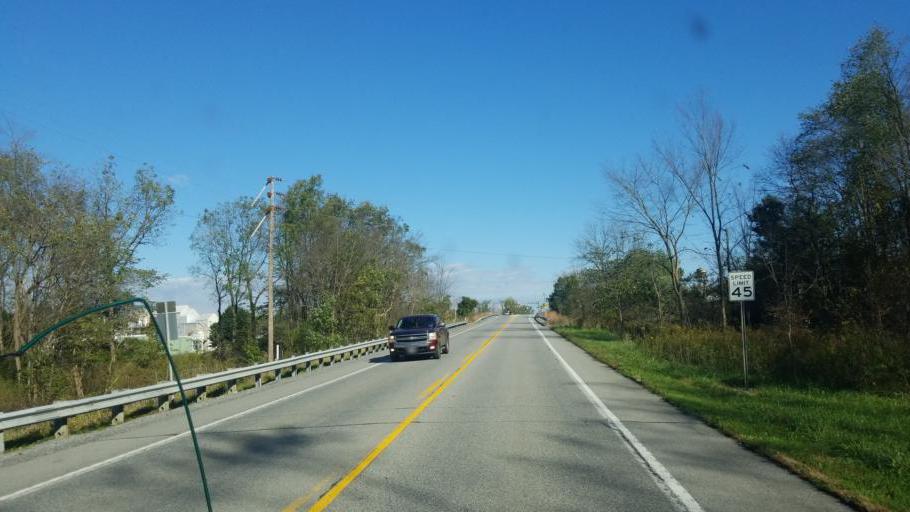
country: US
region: Pennsylvania
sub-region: Blair County
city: Claysburg
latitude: 40.2686
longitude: -78.4603
